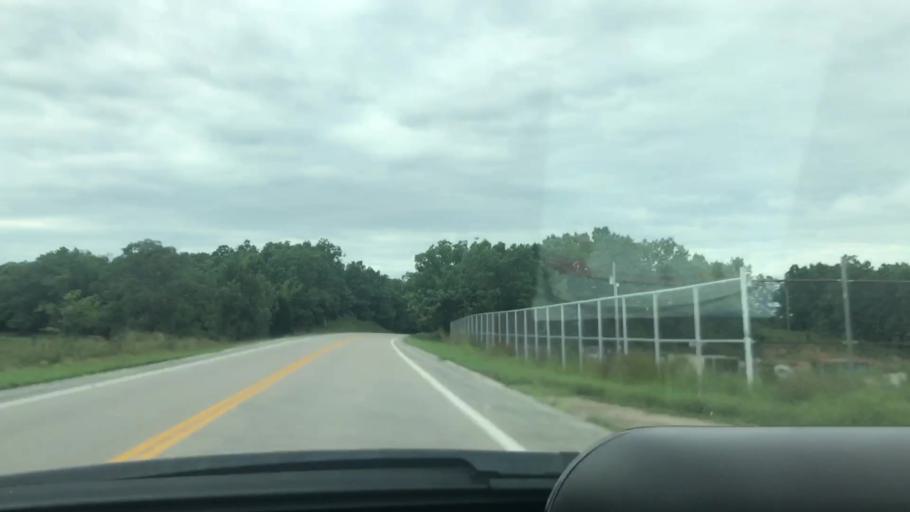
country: US
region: Missouri
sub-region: Benton County
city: Warsaw
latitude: 38.1646
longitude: -93.3065
